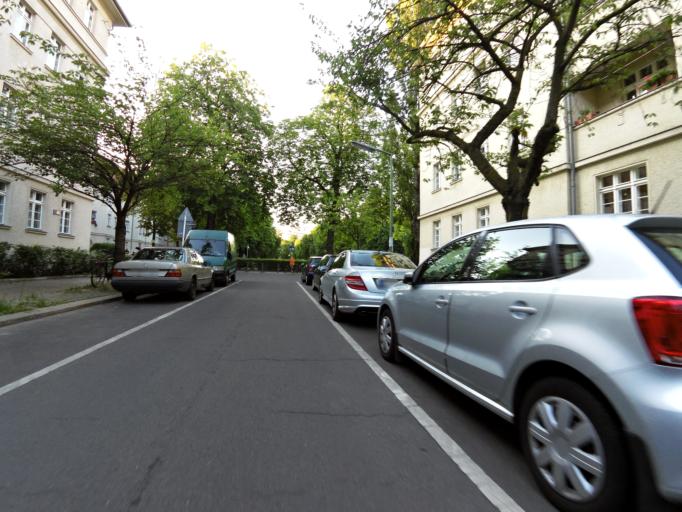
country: DE
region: Berlin
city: Schoneberg Bezirk
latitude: 52.4730
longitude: 13.3416
